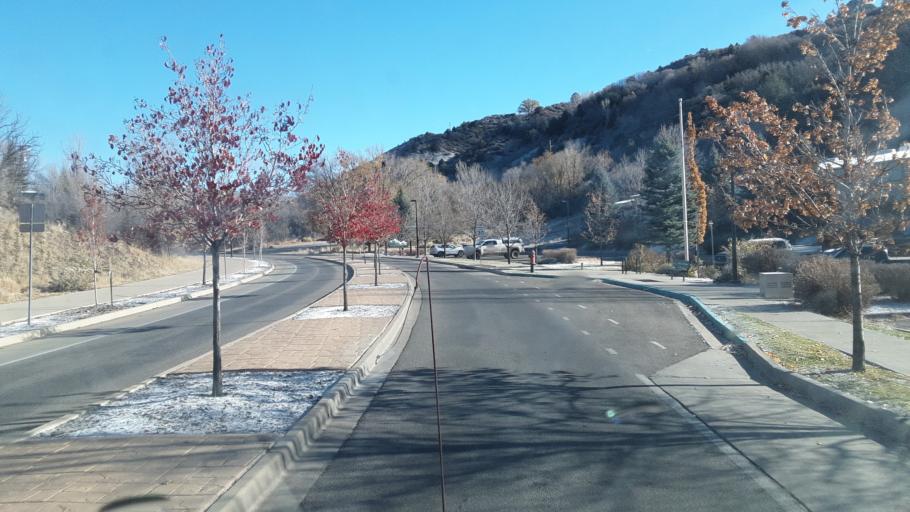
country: US
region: Colorado
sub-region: La Plata County
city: Durango
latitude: 37.2834
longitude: -107.8685
